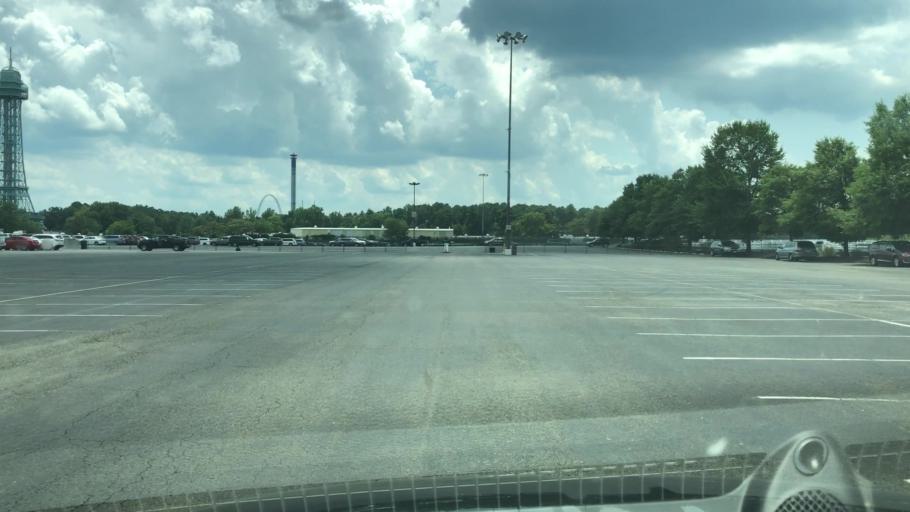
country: US
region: Virginia
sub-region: Hanover County
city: Ashland
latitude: 37.8439
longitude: -77.4478
